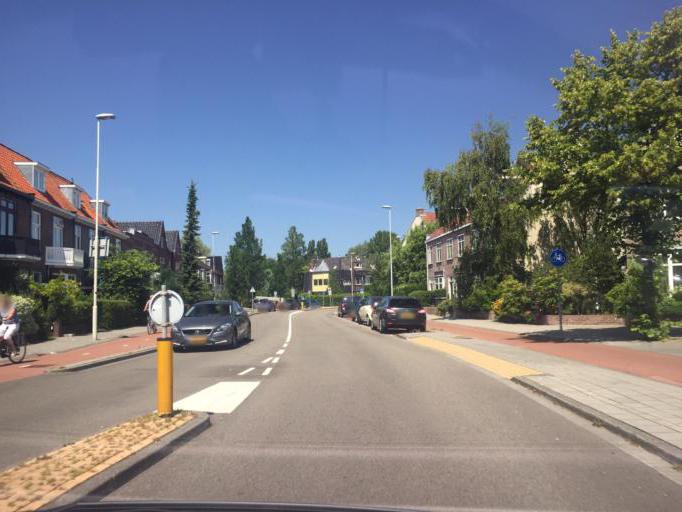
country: NL
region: North Holland
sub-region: Gemeente Bloemendaal
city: Bloemendaal
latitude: 52.3916
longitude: 4.6253
